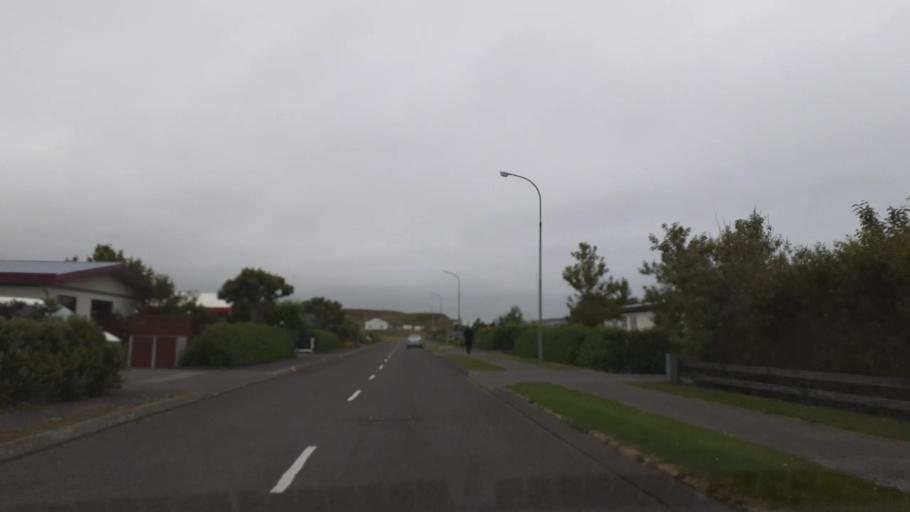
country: IS
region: Northwest
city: Saudarkrokur
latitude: 65.6576
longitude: -20.3042
